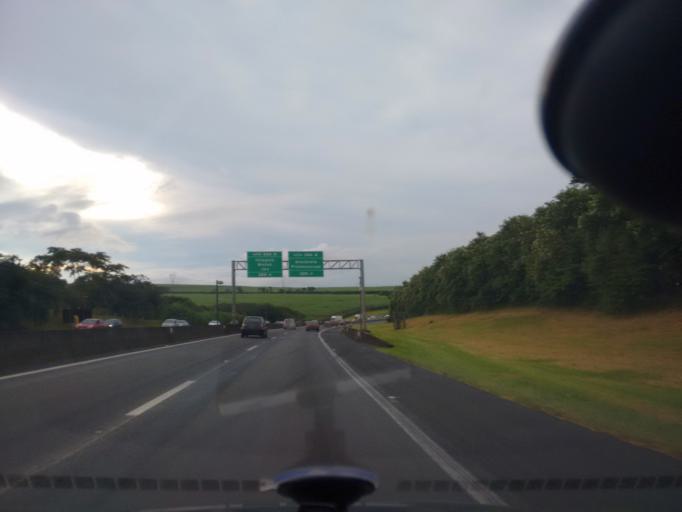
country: BR
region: Sao Paulo
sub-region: Itirapina
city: Itirapina
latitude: -22.2213
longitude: -47.7614
